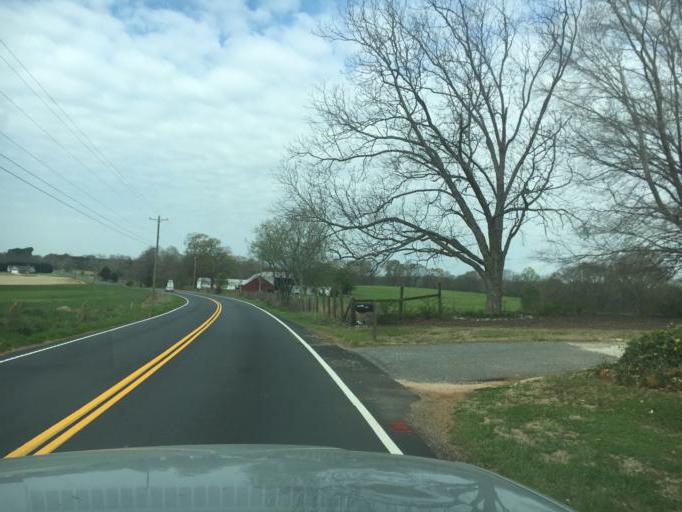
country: US
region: South Carolina
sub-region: Spartanburg County
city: Inman Mills
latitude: 35.0304
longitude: -82.1032
